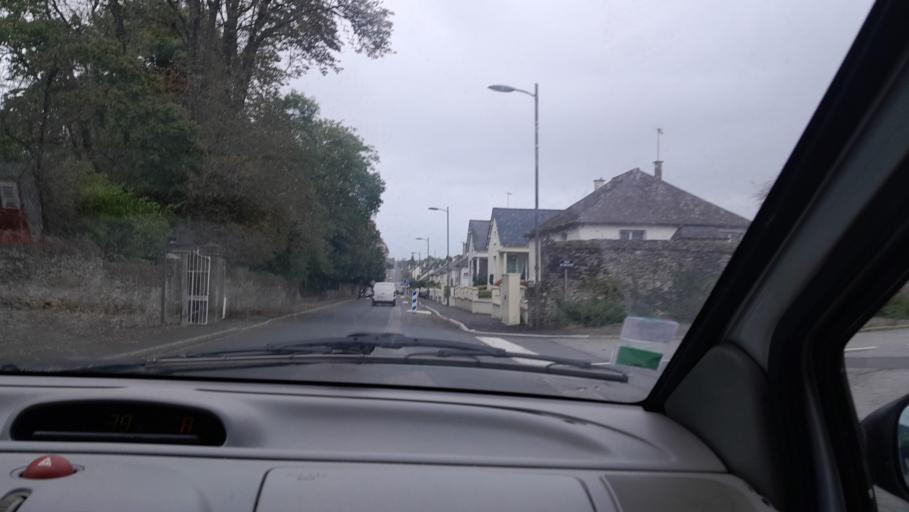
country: FR
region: Pays de la Loire
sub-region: Departement de Maine-et-Loire
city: Pouance
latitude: 47.7432
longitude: -1.1762
